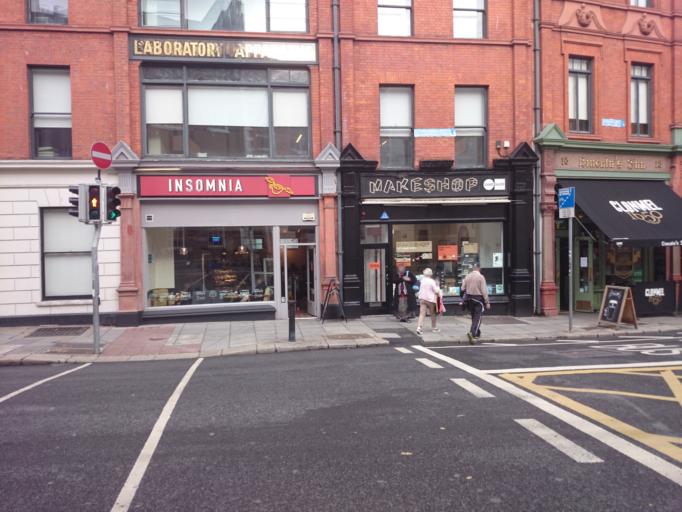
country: IE
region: Leinster
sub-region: Dublin City
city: Dublin
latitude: 53.3417
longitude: -6.2529
